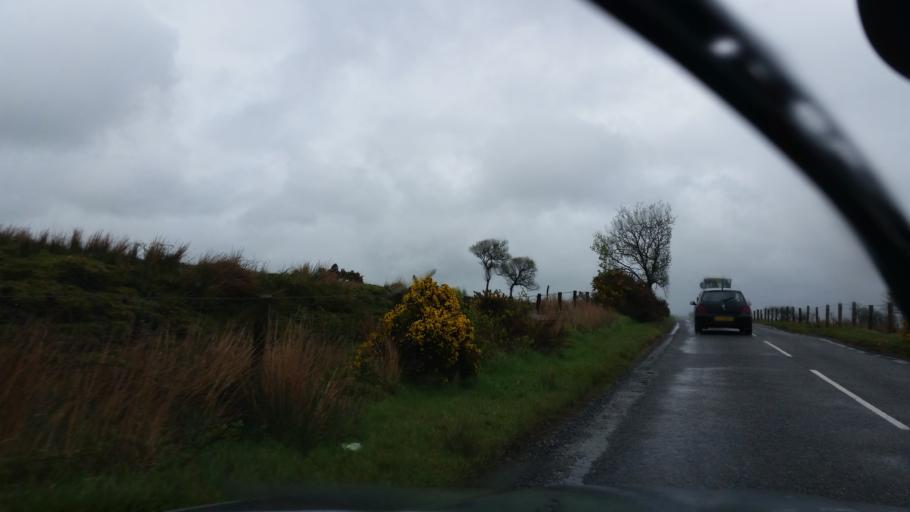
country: GB
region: Northern Ireland
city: Fintona
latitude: 54.4558
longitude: -7.3251
